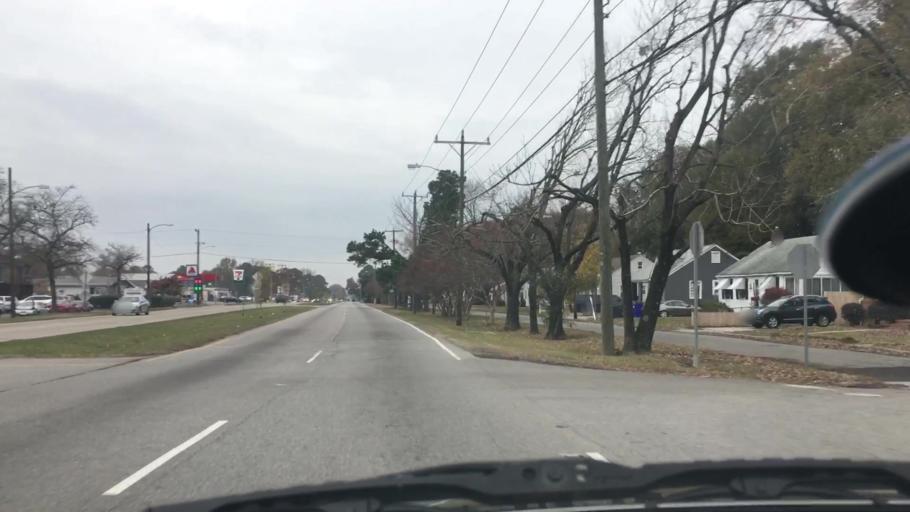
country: US
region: Virginia
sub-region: City of Norfolk
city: Norfolk
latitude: 36.8748
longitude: -76.2167
